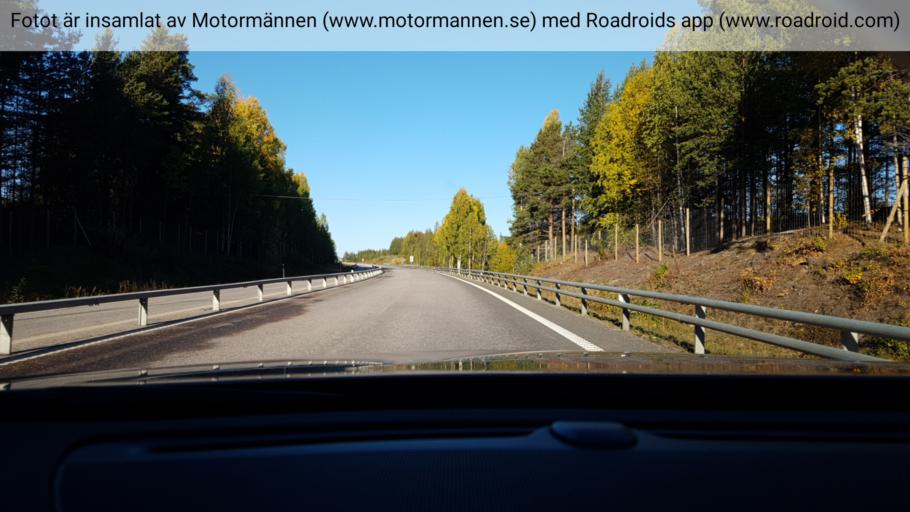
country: SE
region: Norrbotten
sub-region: Pitea Kommun
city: Bergsviken
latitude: 65.3163
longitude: 21.3895
